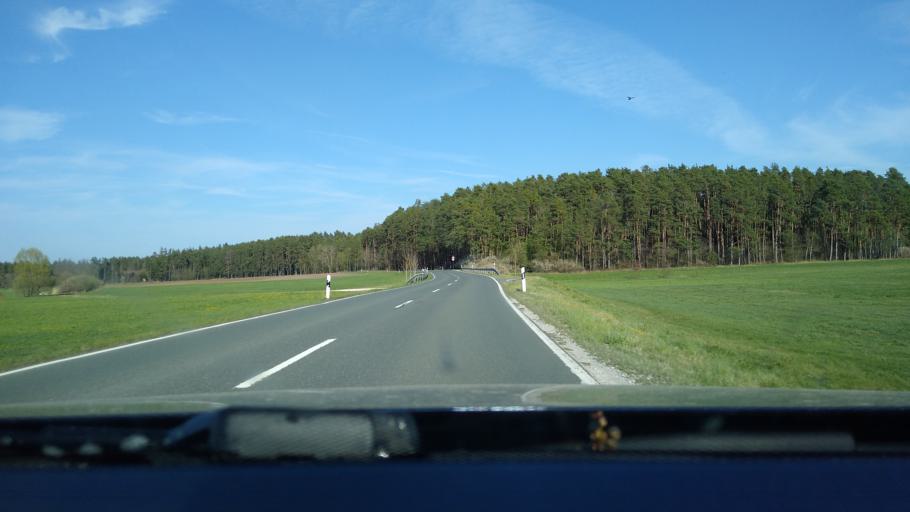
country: DE
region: Bavaria
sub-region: Regierungsbezirk Mittelfranken
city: Wolframs-Eschenbach
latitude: 49.1964
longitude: 10.7346
